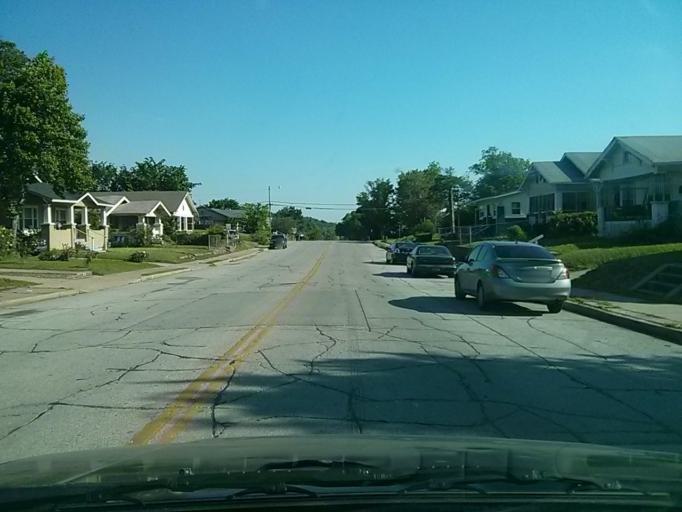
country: US
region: Oklahoma
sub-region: Tulsa County
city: Tulsa
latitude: 36.1723
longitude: -95.9968
